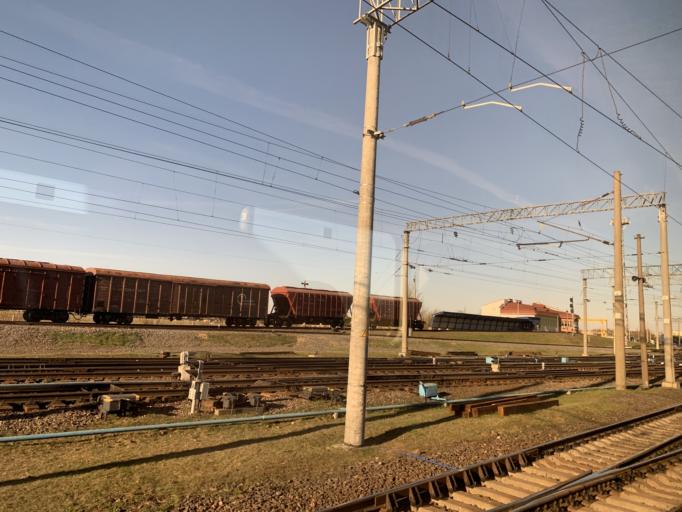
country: BY
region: Minsk
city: Maladzyechna
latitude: 54.3169
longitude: 26.8199
